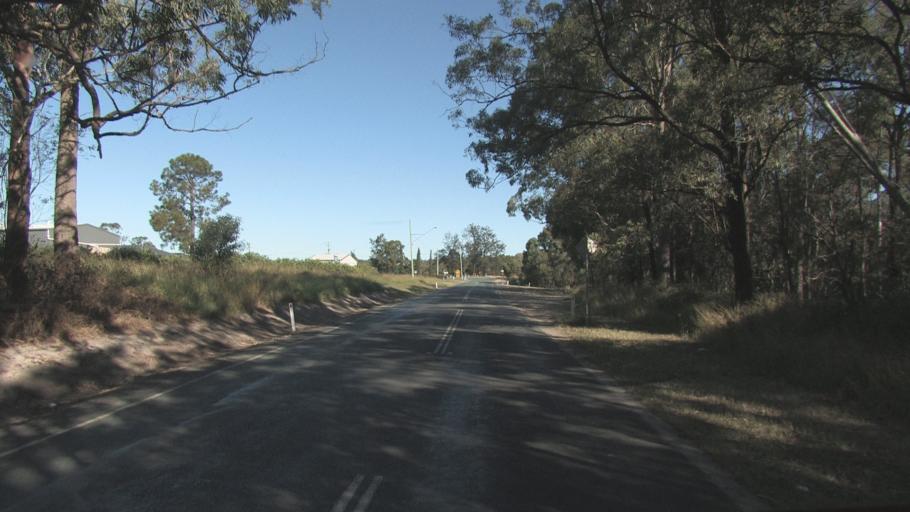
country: AU
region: Queensland
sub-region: Logan
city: Logan Reserve
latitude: -27.7496
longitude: 153.1311
